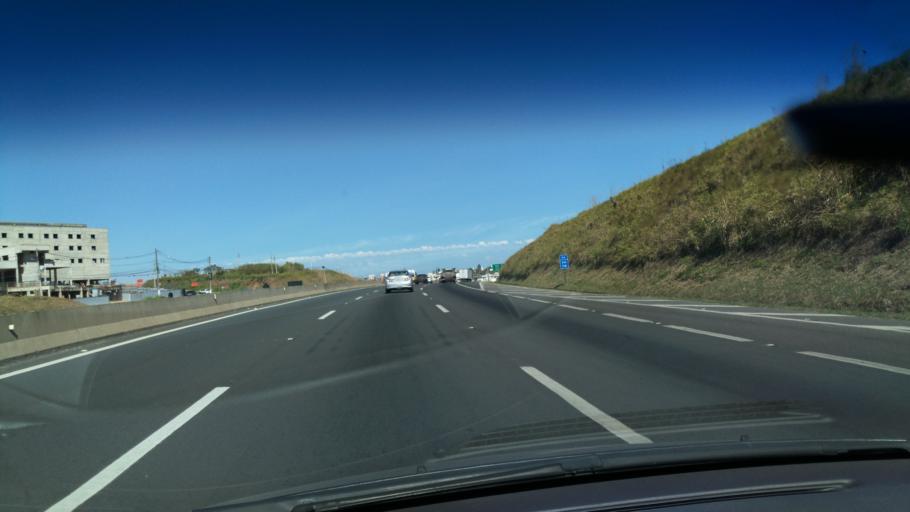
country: BR
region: Sao Paulo
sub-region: Campinas
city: Campinas
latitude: -22.8302
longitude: -47.0331
